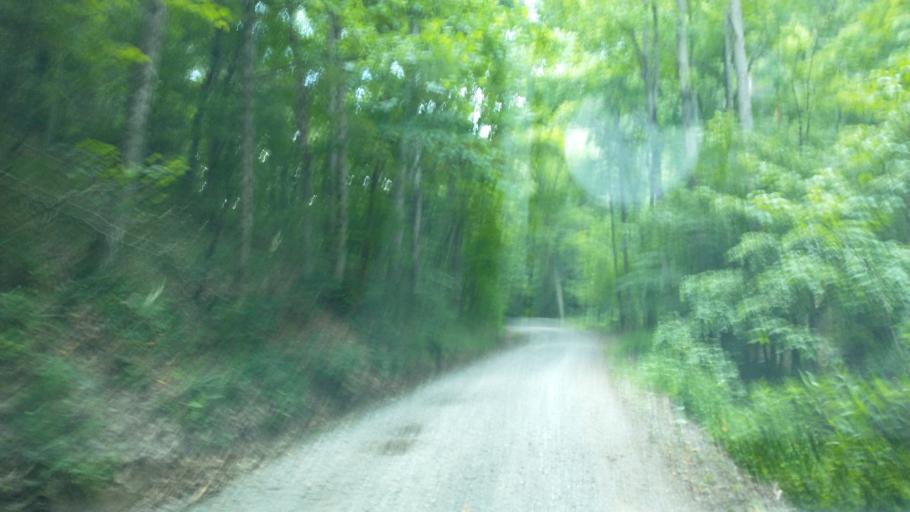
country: US
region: West Virginia
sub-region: Mercer County
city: Athens
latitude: 37.4292
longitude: -80.9969
